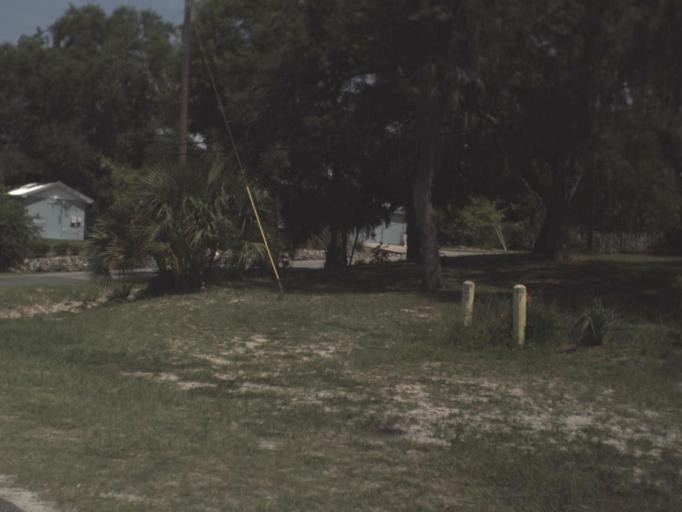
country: US
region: Florida
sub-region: Taylor County
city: Steinhatchee
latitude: 29.6683
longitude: -83.3762
